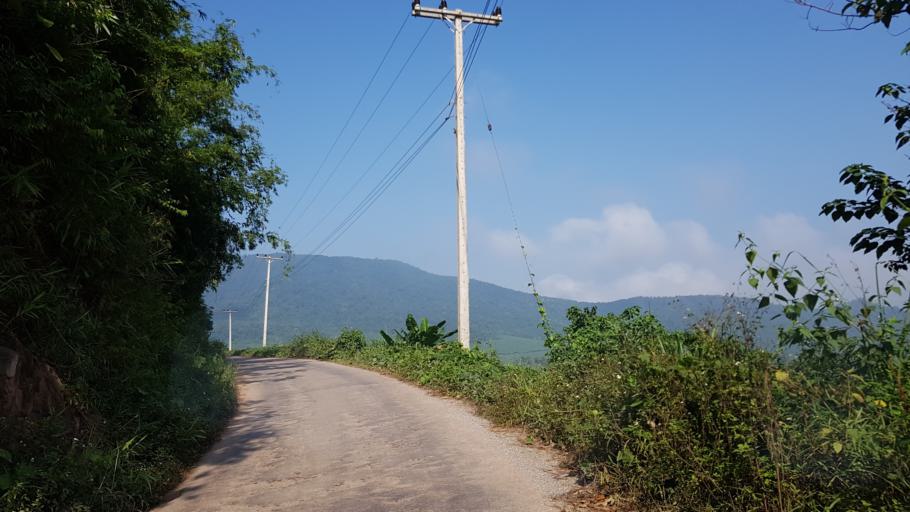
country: LA
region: Oudomxai
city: Muang Xay
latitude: 20.7152
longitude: 102.0940
